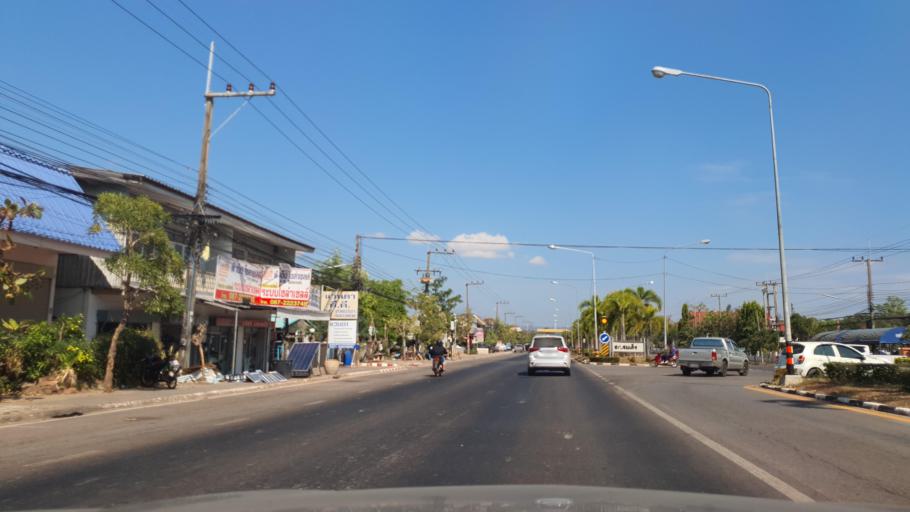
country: TH
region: Kalasin
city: Somdet
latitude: 16.7035
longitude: 103.7479
